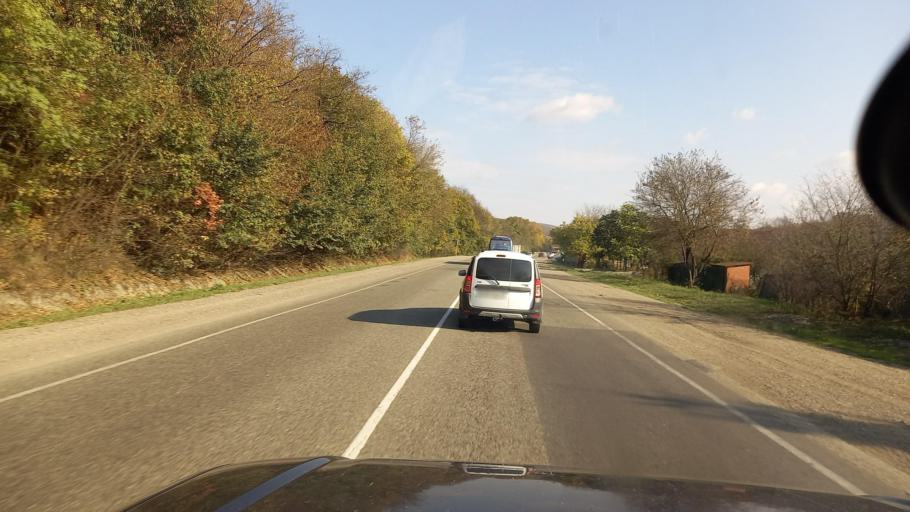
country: RU
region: Krasnodarskiy
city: Verkhnebakanskiy
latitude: 44.8547
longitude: 37.7306
